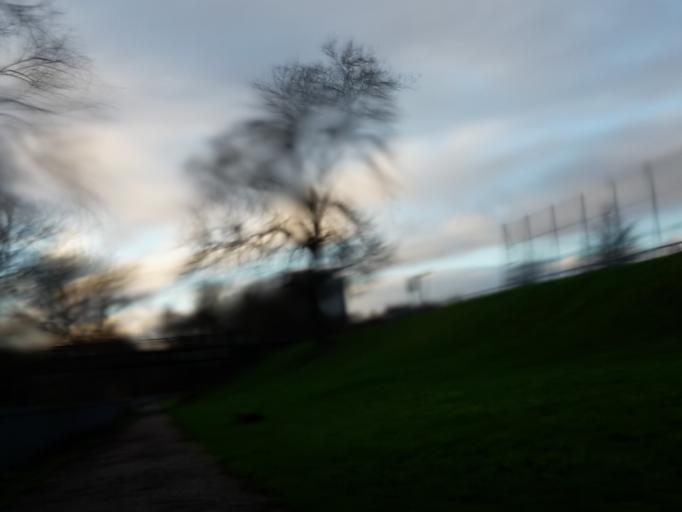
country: GB
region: Scotland
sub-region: South Lanarkshire
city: Rutherglen
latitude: 55.8429
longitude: -4.2341
